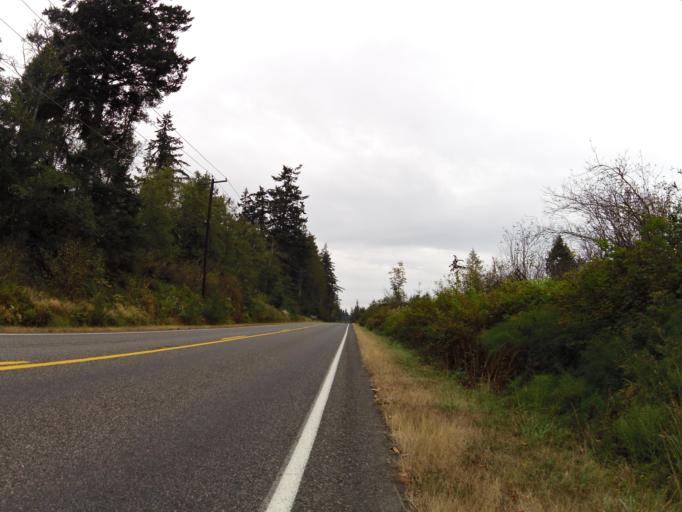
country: US
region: Washington
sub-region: Jefferson County
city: Port Ludlow
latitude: 47.9774
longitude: -122.7106
